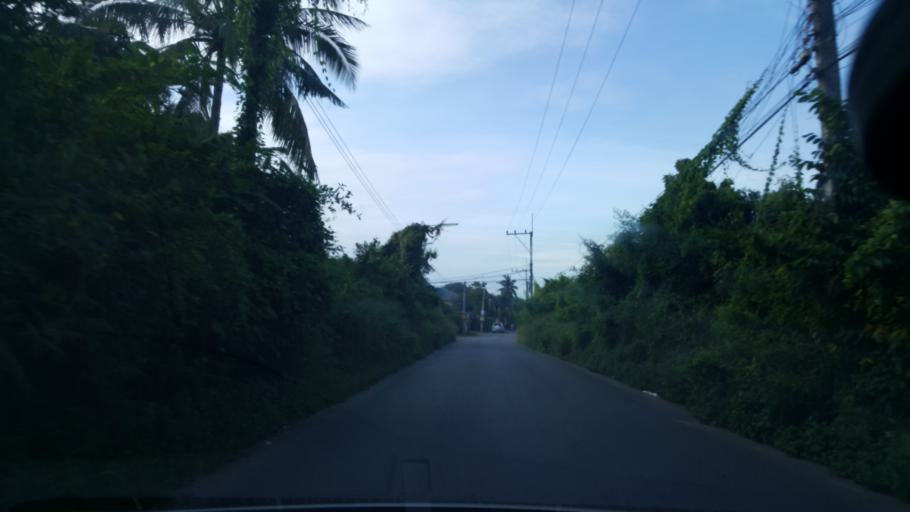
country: TH
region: Chon Buri
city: Sattahip
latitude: 12.6795
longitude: 100.9106
